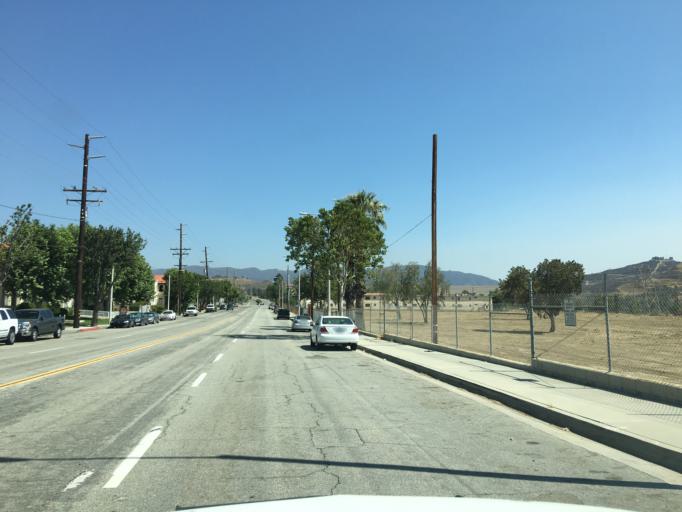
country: US
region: California
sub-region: Los Angeles County
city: Castaic
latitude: 34.4934
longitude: -118.6166
